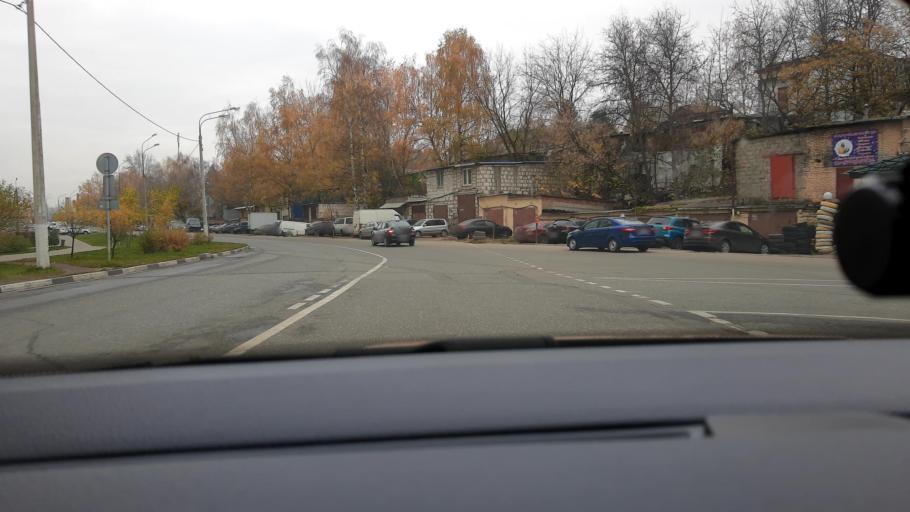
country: RU
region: Moskovskaya
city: Cherkizovo
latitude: 55.9441
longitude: 37.7737
